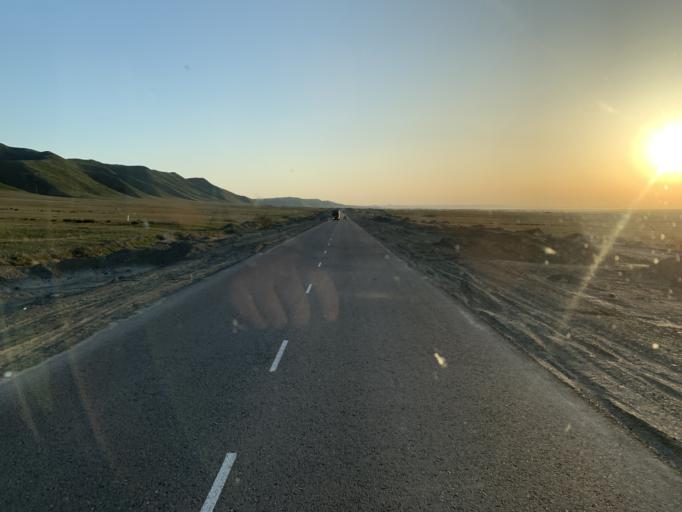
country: KZ
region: Almaty Oblysy
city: Matay
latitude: 45.3930
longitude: 78.7989
